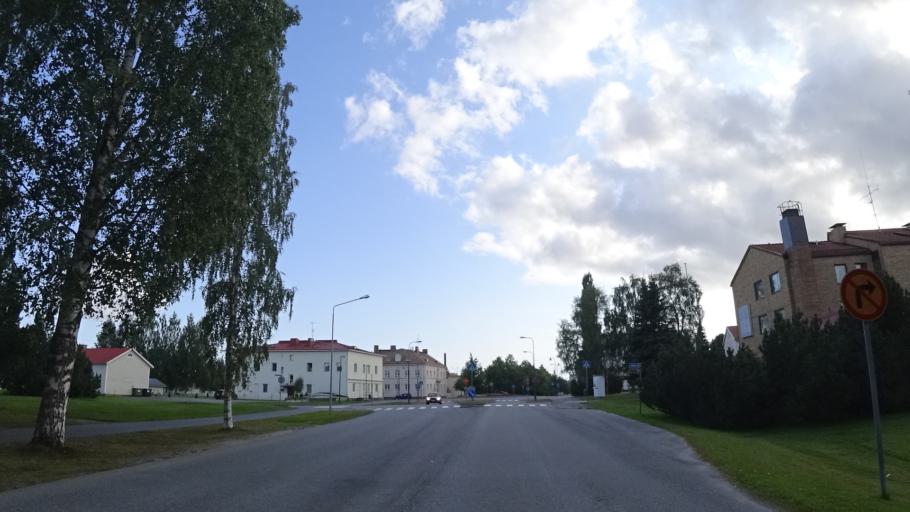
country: FI
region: North Karelia
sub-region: Pielisen Karjala
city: Lieksa
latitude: 63.3208
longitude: 30.0216
